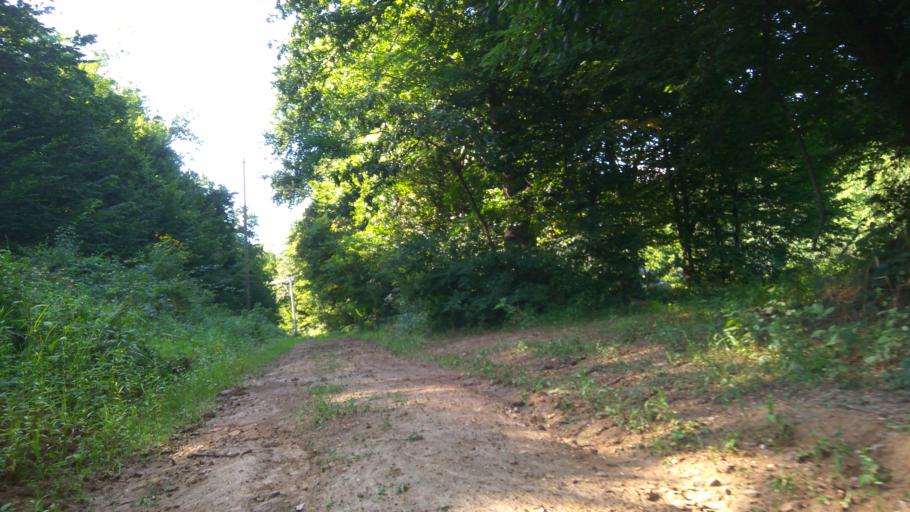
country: SK
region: Nitriansky
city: Sahy
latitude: 47.9897
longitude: 18.9647
